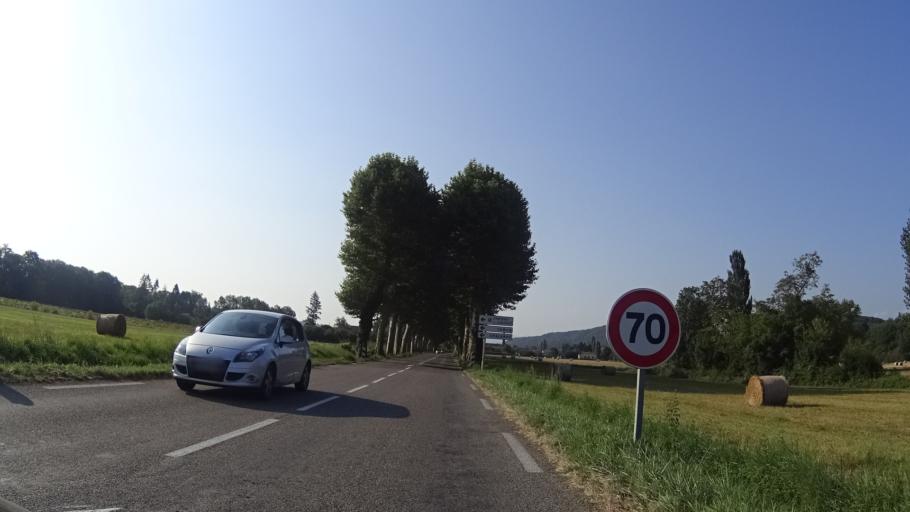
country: FR
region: Midi-Pyrenees
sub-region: Departement de l'Ariege
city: Mirepoix
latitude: 43.0588
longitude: 1.8833
